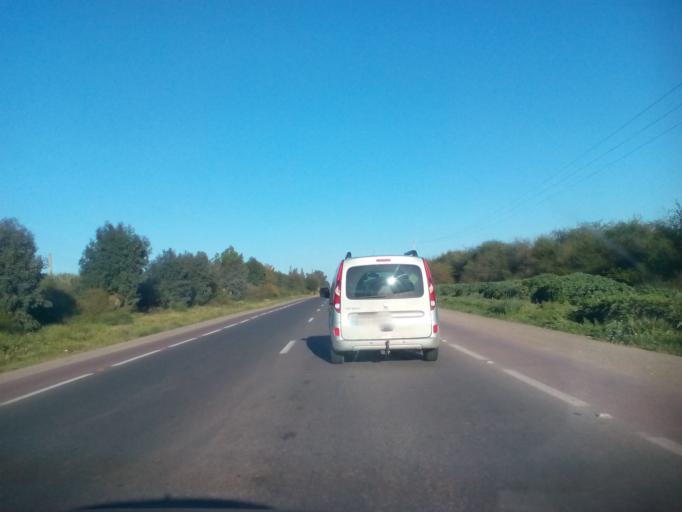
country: MA
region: Marrakech-Tensift-Al Haouz
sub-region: Marrakech
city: Marrakesh
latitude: 31.6294
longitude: -8.1384
